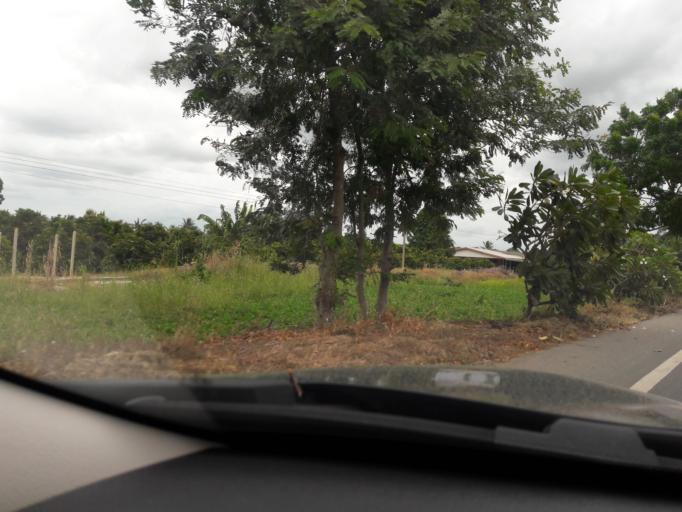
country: TH
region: Ratchaburi
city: Bang Phae
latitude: 13.6066
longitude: 99.9411
